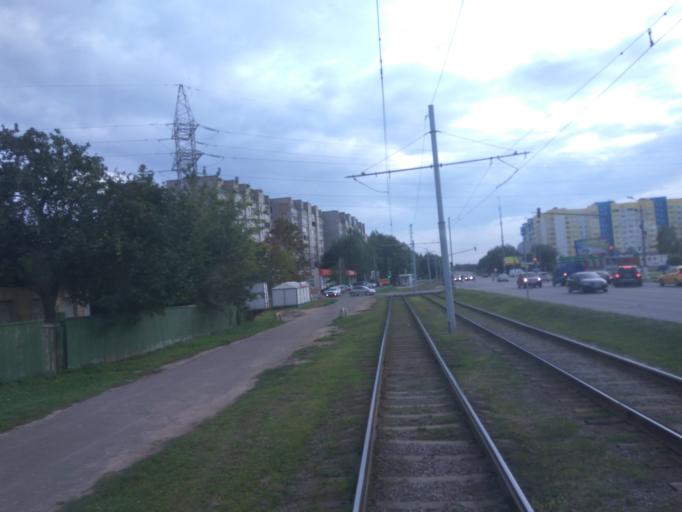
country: RU
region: Moskovskaya
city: Kolomna
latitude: 55.0780
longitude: 38.7620
